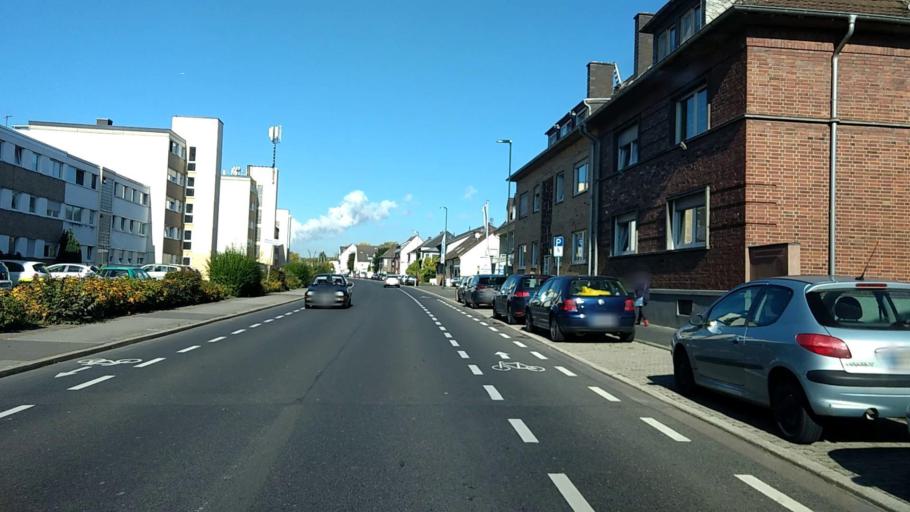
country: DE
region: North Rhine-Westphalia
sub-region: Regierungsbezirk Koln
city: Kerpen
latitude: 50.9194
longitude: 6.7078
